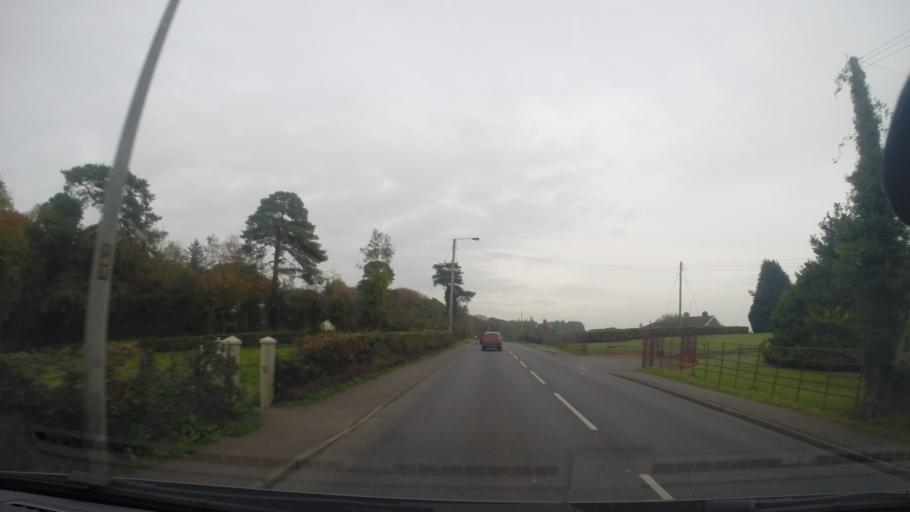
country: GB
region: Northern Ireland
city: Fivemiletown
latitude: 54.3798
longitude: -7.3061
